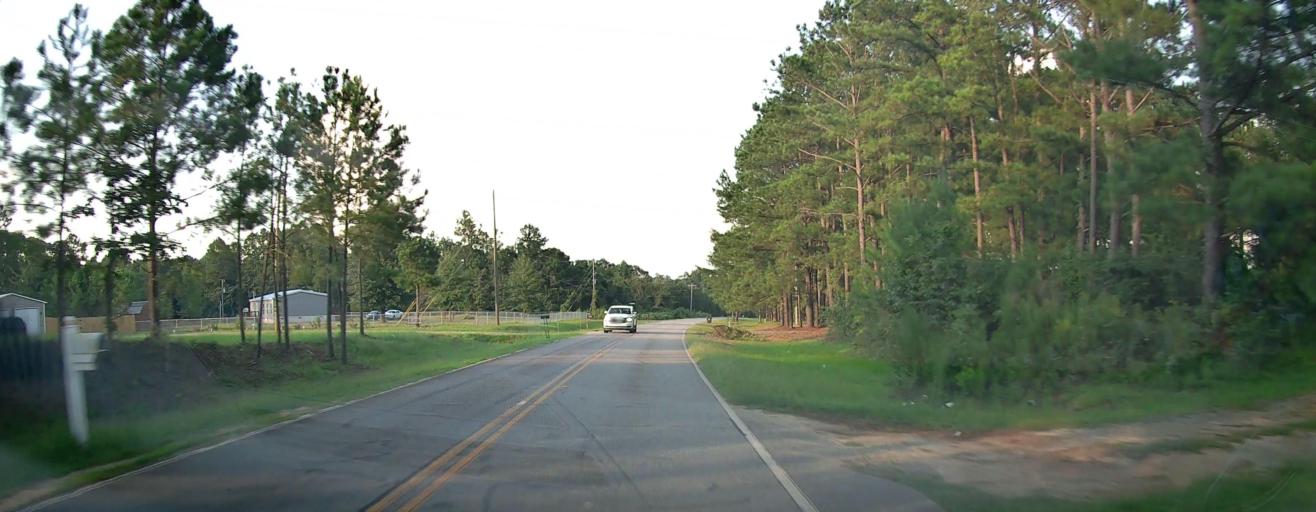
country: US
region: Georgia
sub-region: Peach County
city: Byron
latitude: 32.6203
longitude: -83.8274
